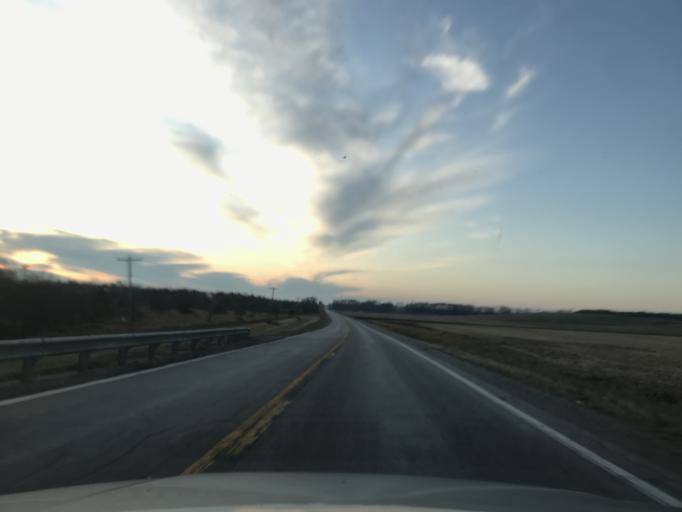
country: US
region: Illinois
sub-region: Henderson County
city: Oquawka
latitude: 41.0191
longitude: -90.8108
